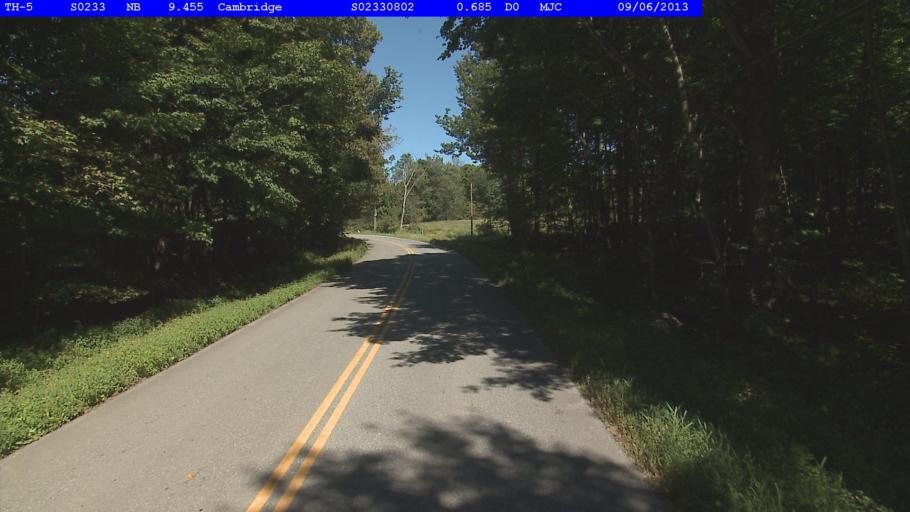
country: US
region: Vermont
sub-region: Chittenden County
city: Jericho
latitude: 44.5931
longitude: -72.8598
